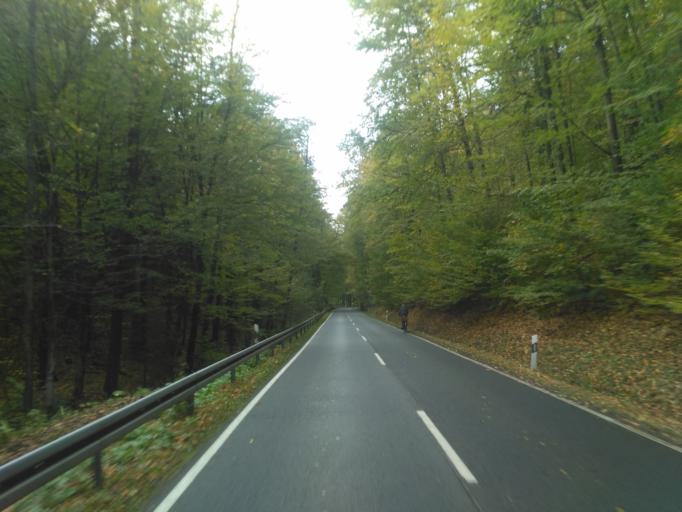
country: DE
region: Saxony
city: Sebnitz
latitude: 50.9622
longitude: 14.2217
